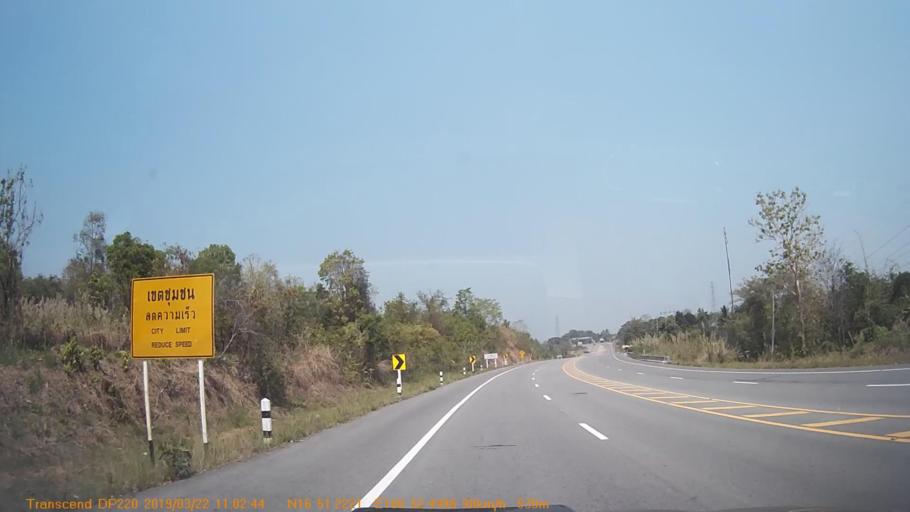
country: TH
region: Phetchabun
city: Khao Kho
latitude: 16.8537
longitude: 100.8742
